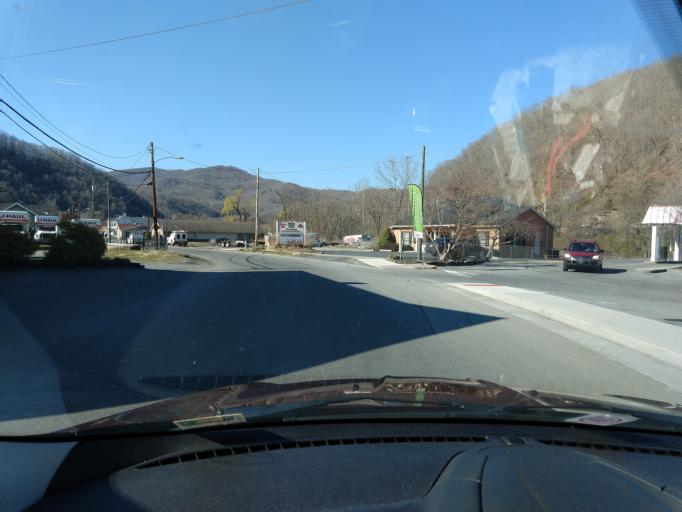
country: US
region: West Virginia
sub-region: Summers County
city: Hinton
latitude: 37.6606
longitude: -80.8918
